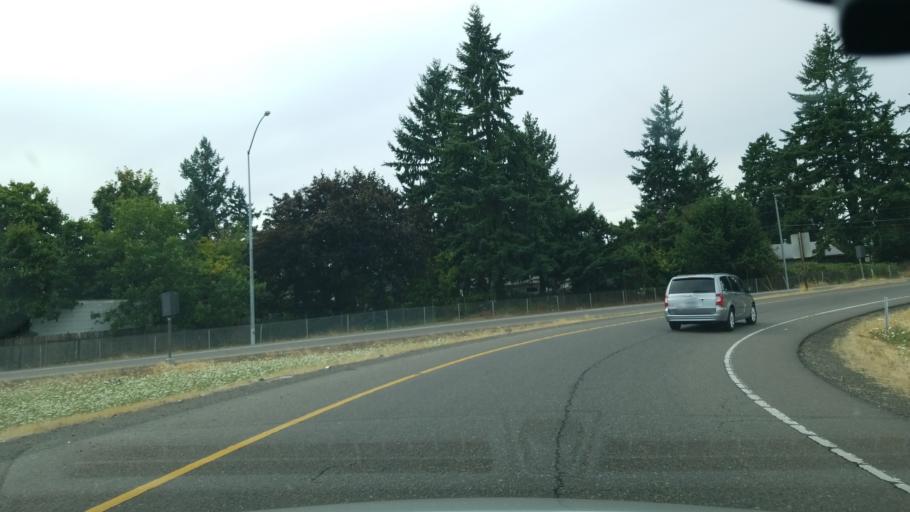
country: US
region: Oregon
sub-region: Clackamas County
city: Clackamas
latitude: 45.4055
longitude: -122.5723
